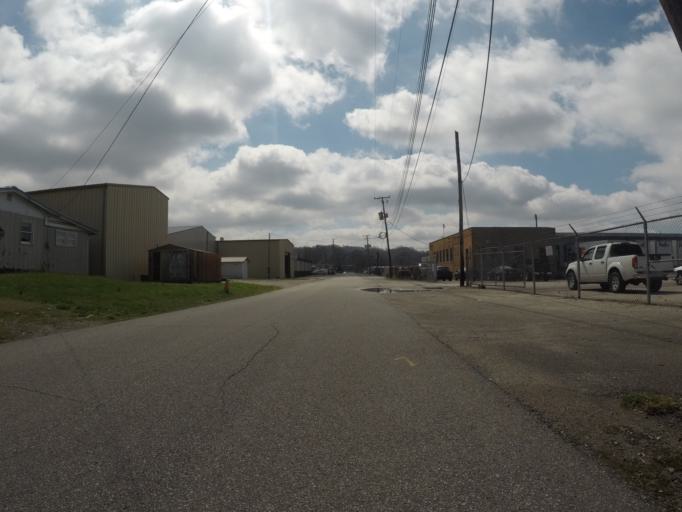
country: US
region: West Virginia
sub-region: Wayne County
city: Ceredo
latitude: 38.3993
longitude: -82.5658
